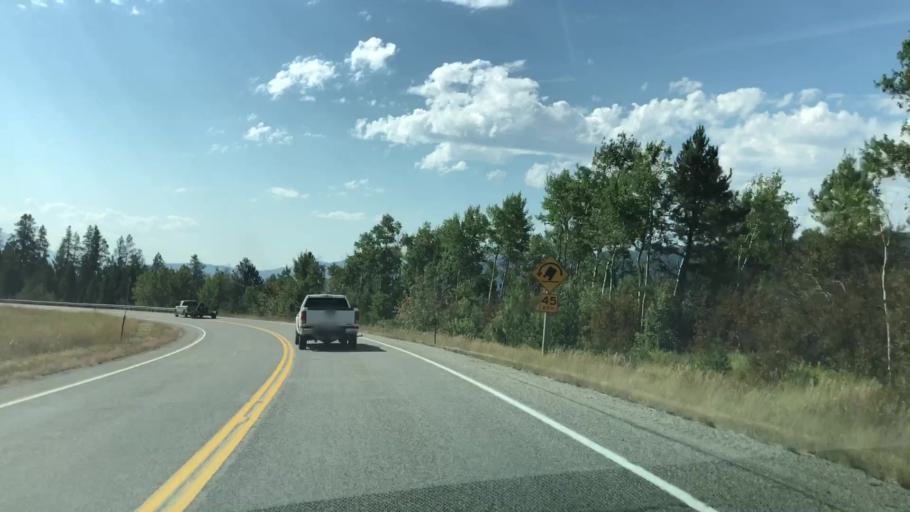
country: US
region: Wyoming
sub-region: Teton County
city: Hoback
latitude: 43.2525
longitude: -111.1172
